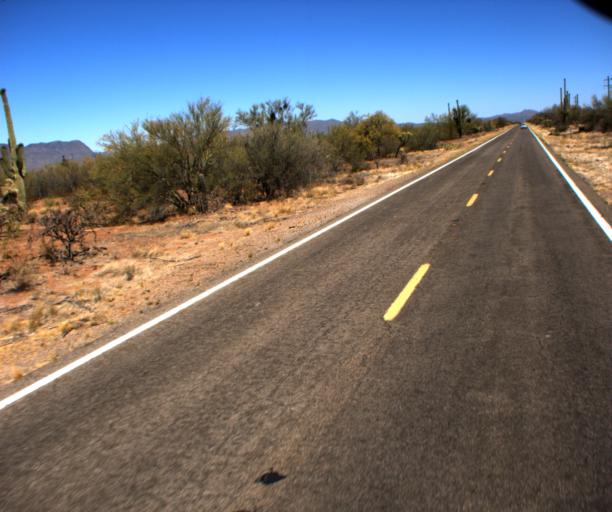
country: US
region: Arizona
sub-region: Pima County
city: Sells
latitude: 32.0448
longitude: -112.0212
